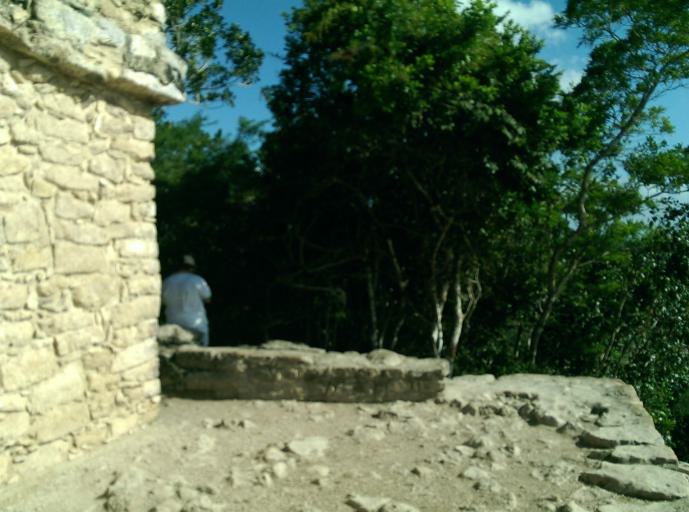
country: MX
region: Quintana Roo
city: Coba
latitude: 20.4948
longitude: -87.7202
